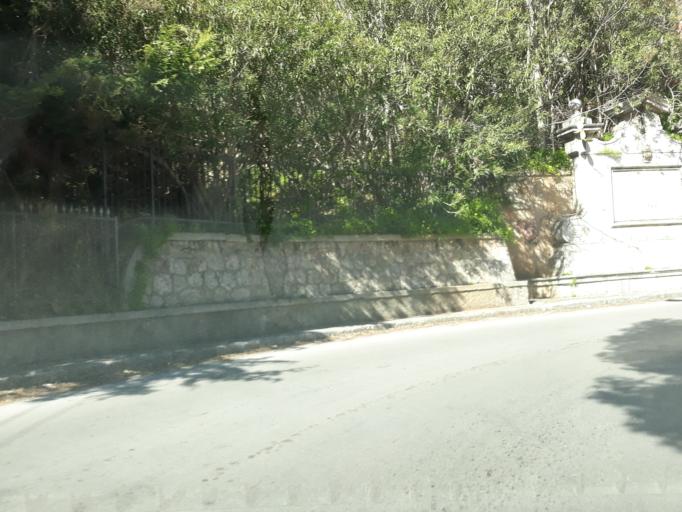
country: IT
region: Sicily
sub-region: Palermo
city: Monreale
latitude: 38.0915
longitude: 13.3047
